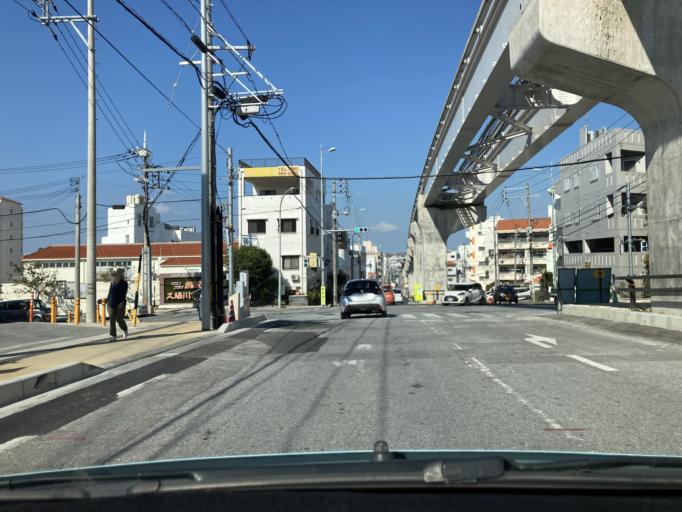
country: JP
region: Okinawa
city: Naha-shi
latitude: 26.2212
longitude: 127.7269
